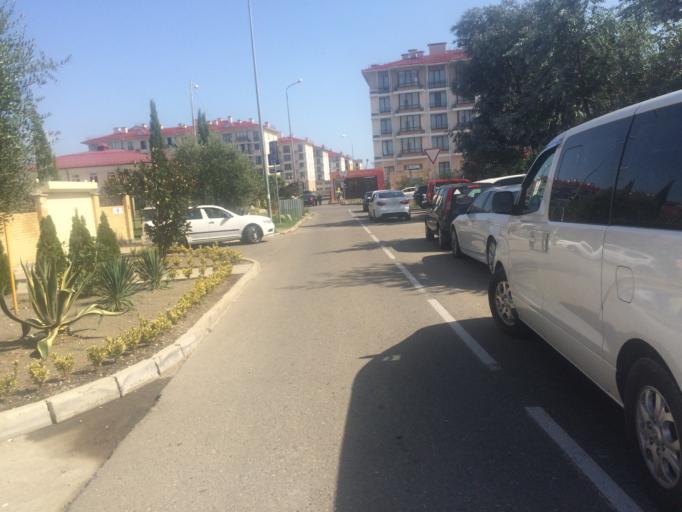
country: RU
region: Krasnodarskiy
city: Adler
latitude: 43.3978
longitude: 39.9742
